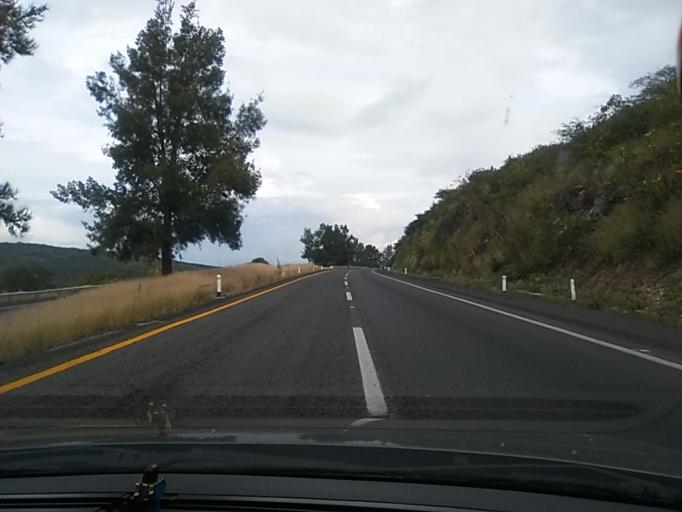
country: MX
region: Michoacan
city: Ixtlan
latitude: 20.2033
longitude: -102.3397
